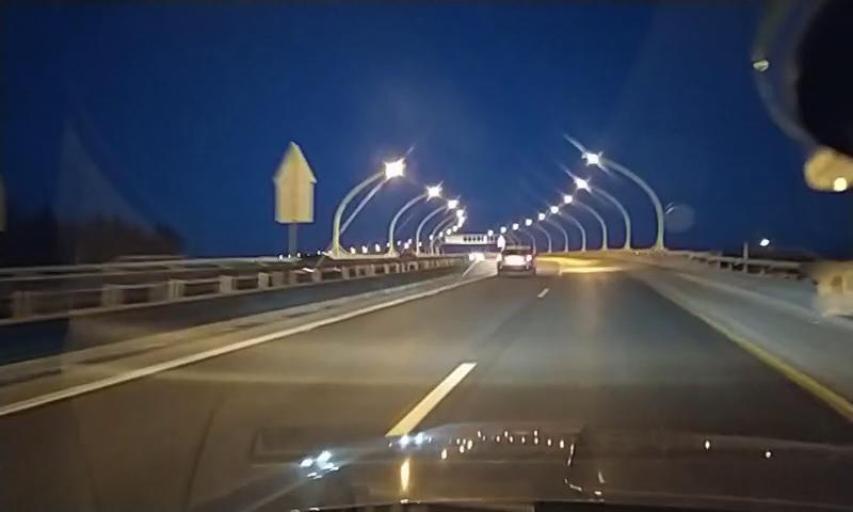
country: RU
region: St.-Petersburg
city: Beloostrov
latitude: 60.1341
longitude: 30.0599
